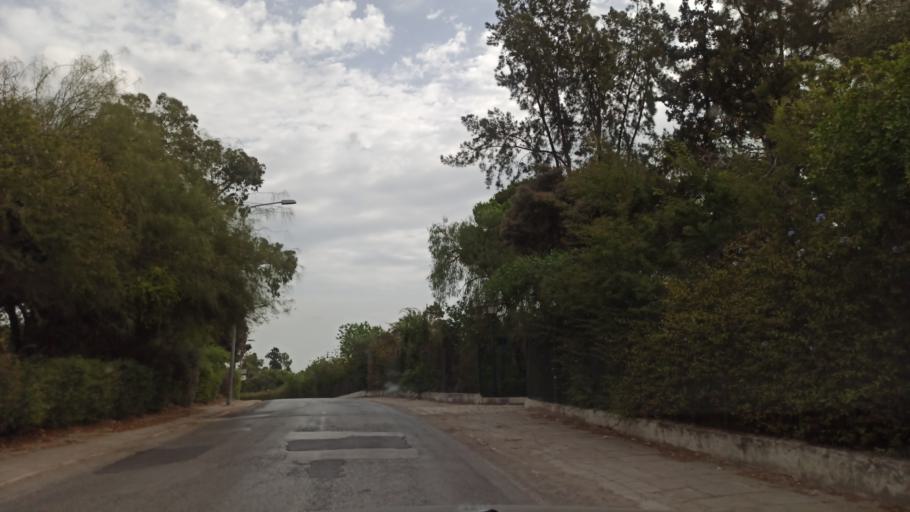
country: TN
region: Tunis
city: Tunis
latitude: 36.8192
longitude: 10.1727
